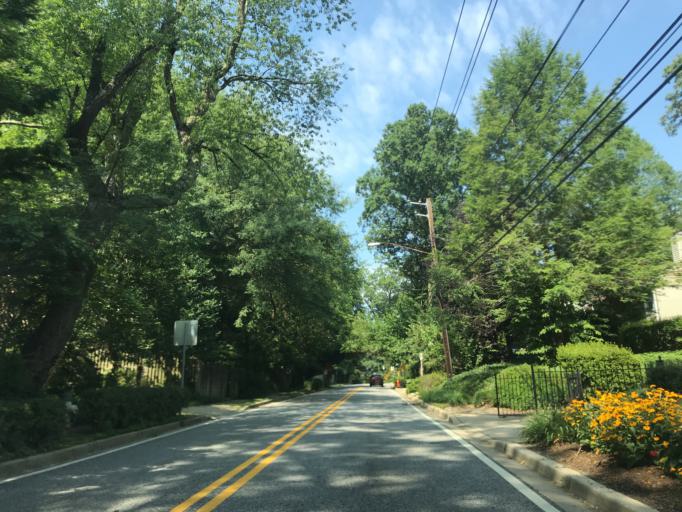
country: US
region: Maryland
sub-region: Montgomery County
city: Bethesda
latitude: 38.9870
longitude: -77.1086
